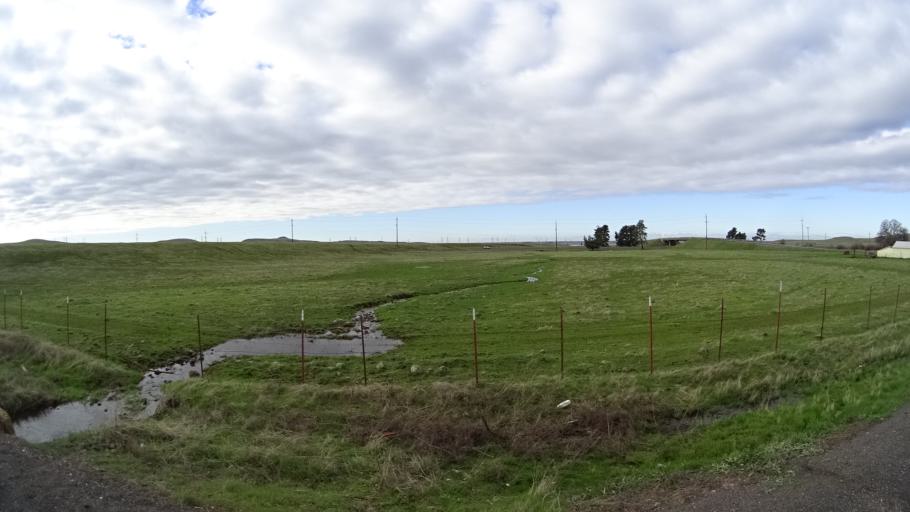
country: US
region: California
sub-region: Butte County
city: Thermalito
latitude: 39.5569
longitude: -121.5972
